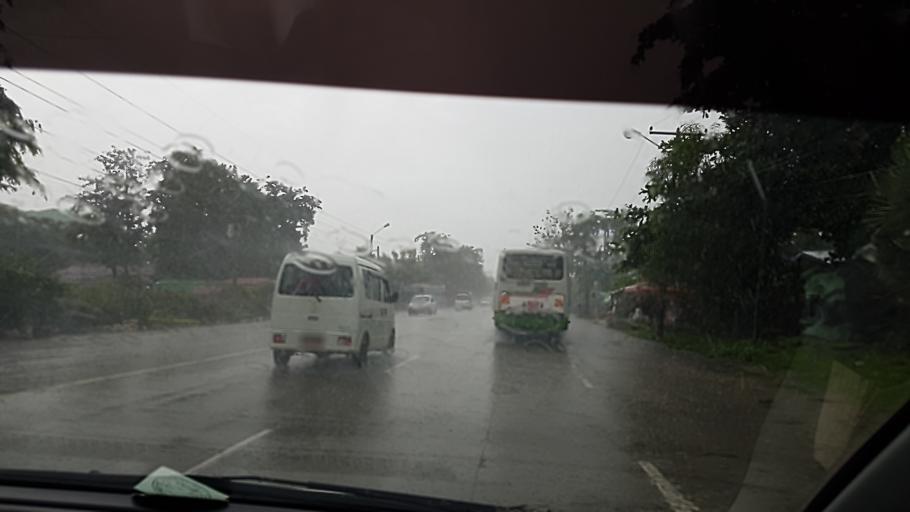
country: MM
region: Yangon
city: Syriam
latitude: 16.7768
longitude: 96.1968
